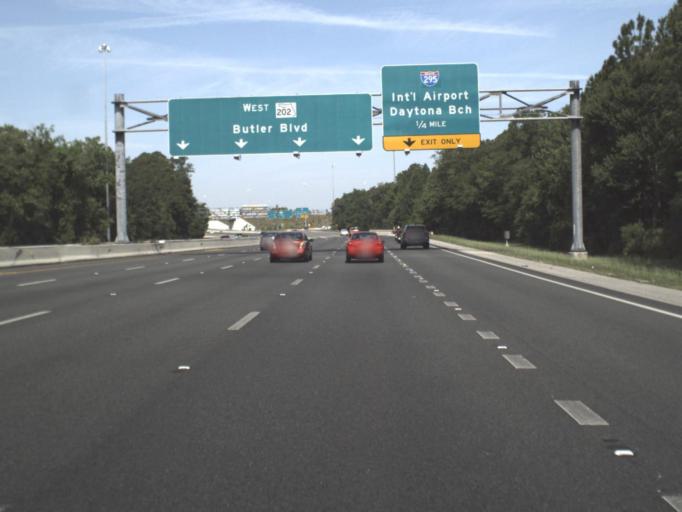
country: US
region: Florida
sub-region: Duval County
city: Jacksonville Beach
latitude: 30.2535
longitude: -81.5051
